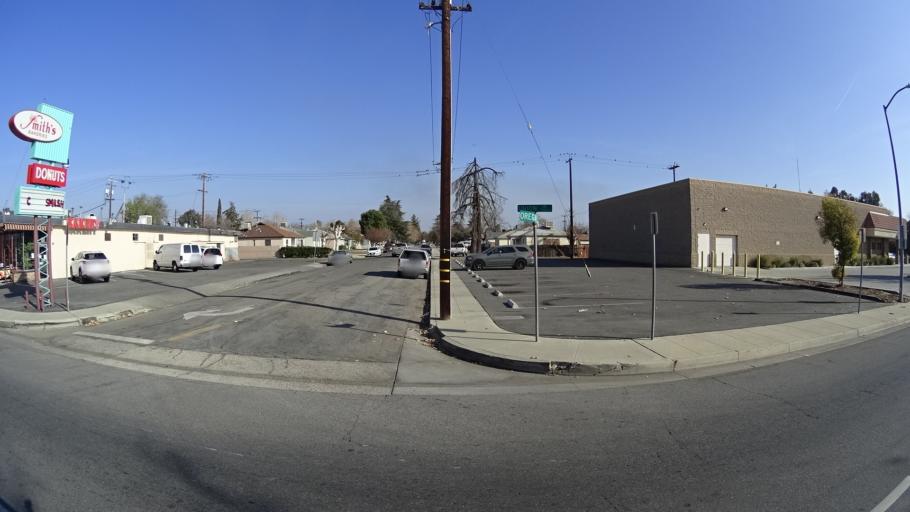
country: US
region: California
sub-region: Kern County
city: Bakersfield
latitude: 35.3848
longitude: -119.0028
